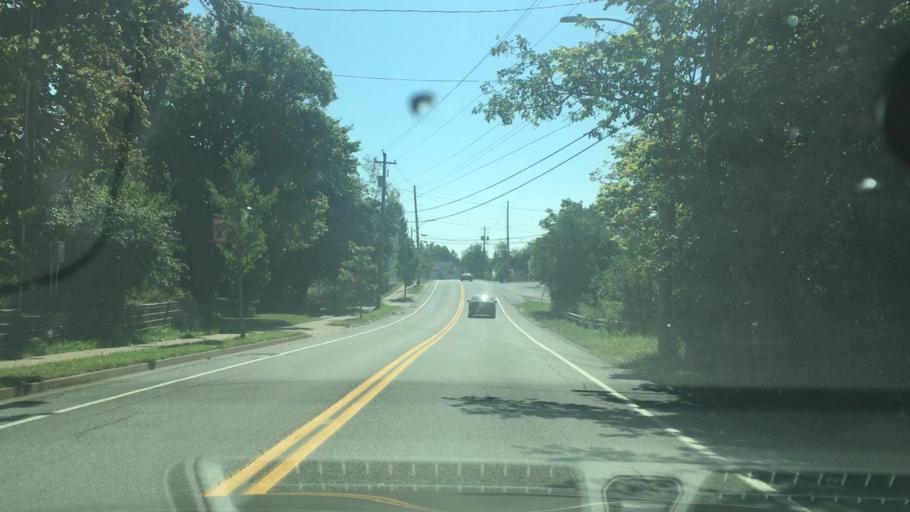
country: CA
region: Nova Scotia
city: New Glasgow
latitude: 44.9265
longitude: -62.5420
